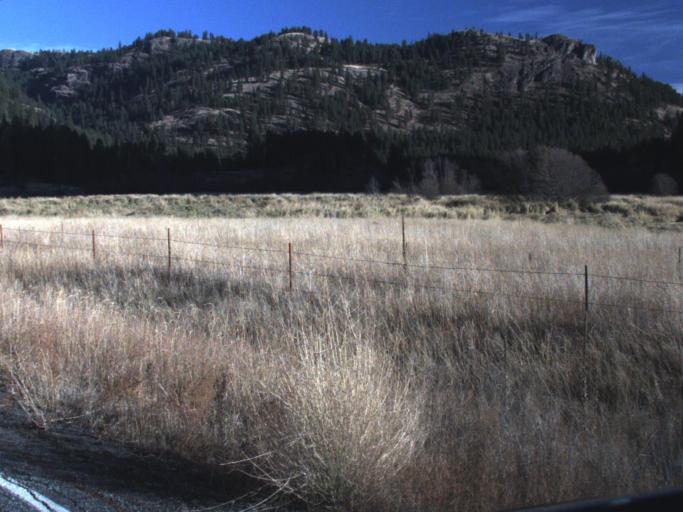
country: US
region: Washington
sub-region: Ferry County
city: Republic
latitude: 48.4625
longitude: -118.7523
